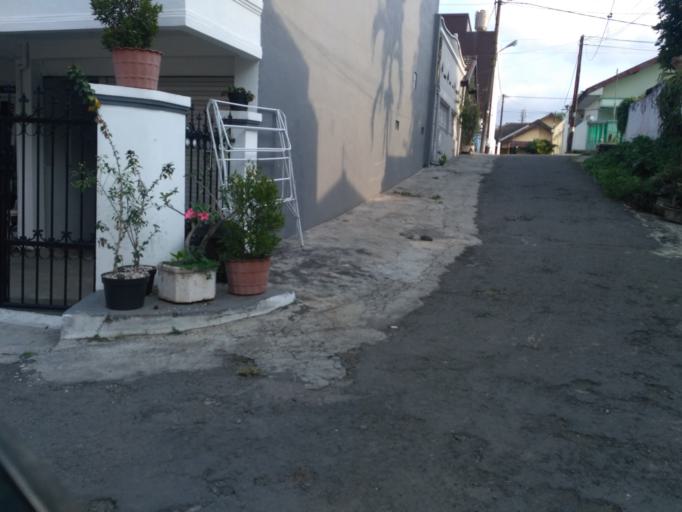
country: ID
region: East Java
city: Malang
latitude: -7.9374
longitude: 112.6324
